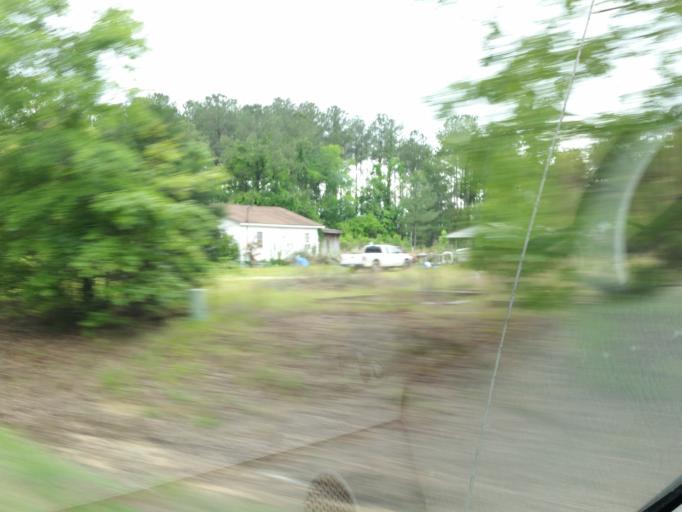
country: US
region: Georgia
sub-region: Crawford County
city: Knoxville
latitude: 32.6758
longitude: -83.9000
